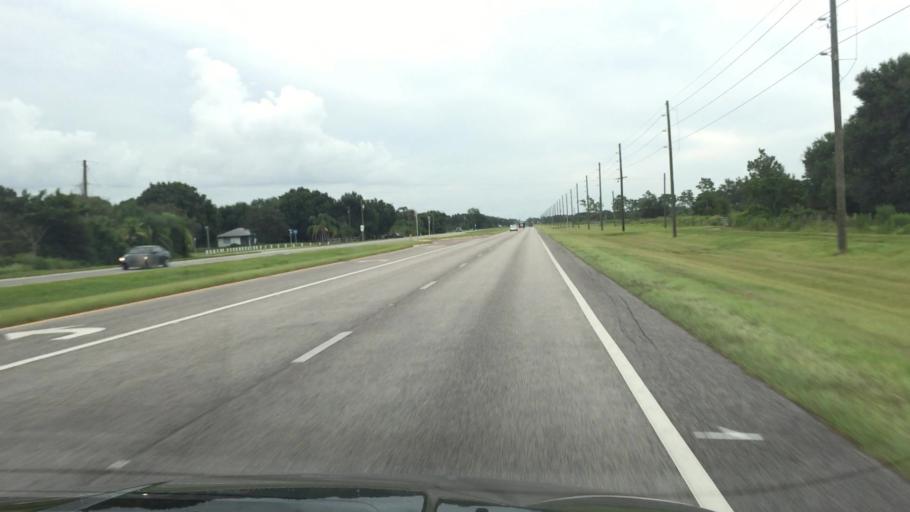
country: US
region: Florida
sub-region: DeSoto County
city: Nocatee
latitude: 27.1361
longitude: -81.8999
